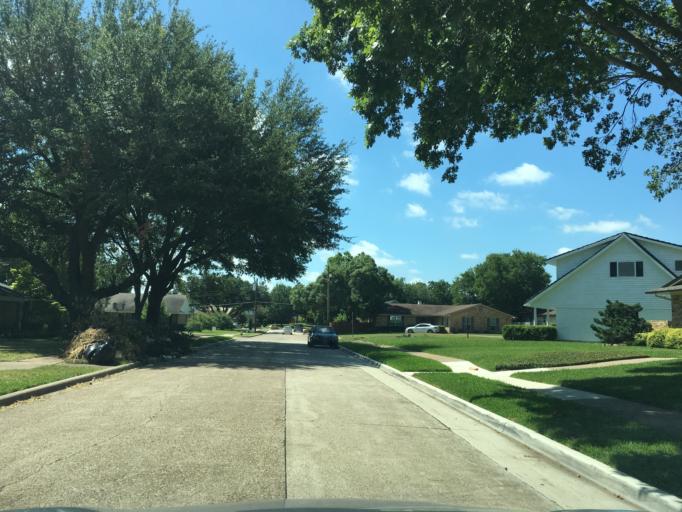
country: US
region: Texas
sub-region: Dallas County
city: Garland
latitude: 32.8483
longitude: -96.6526
